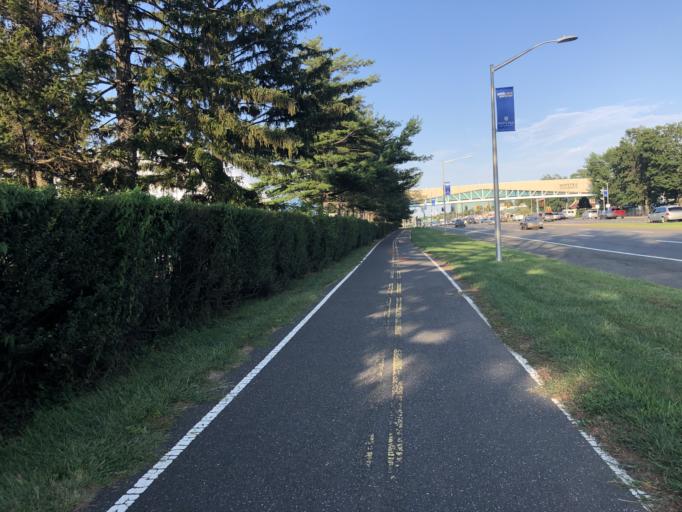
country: US
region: New York
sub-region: Nassau County
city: East Garden City
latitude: 40.7171
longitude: -73.5964
